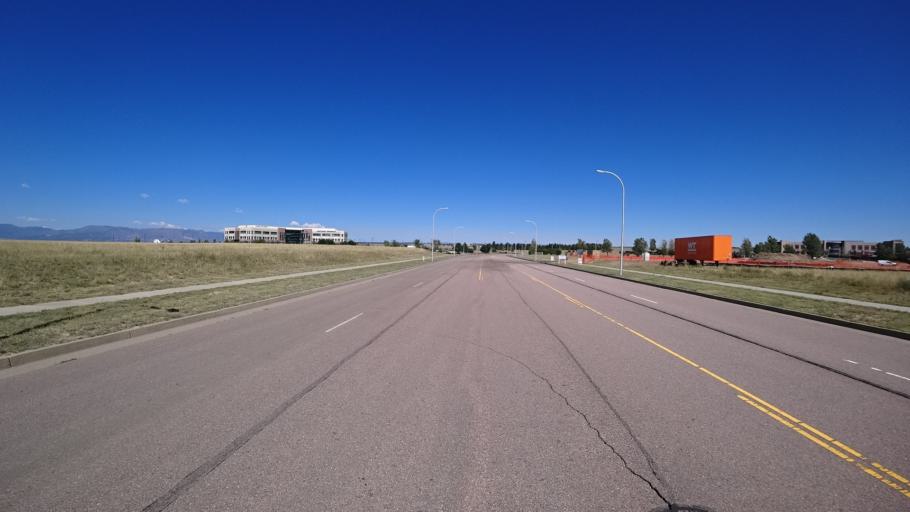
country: US
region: Colorado
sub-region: El Paso County
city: Security-Widefield
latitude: 38.7766
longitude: -104.6999
